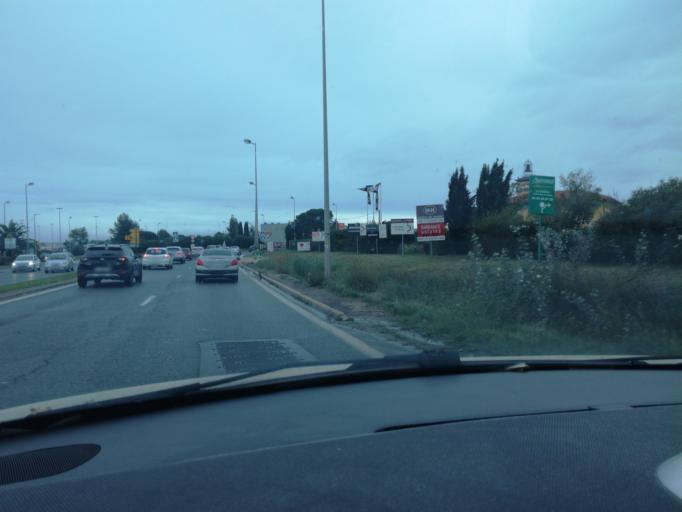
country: FR
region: Provence-Alpes-Cote d'Azur
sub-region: Departement du Var
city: Puget-sur-Argens
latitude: 43.4444
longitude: 6.7005
